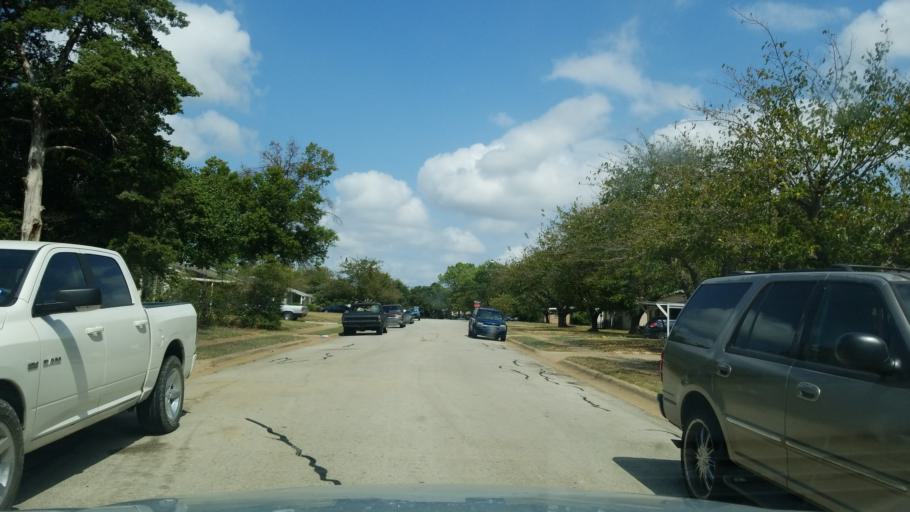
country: US
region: Texas
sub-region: Tarrant County
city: Euless
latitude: 32.8506
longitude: -97.0936
